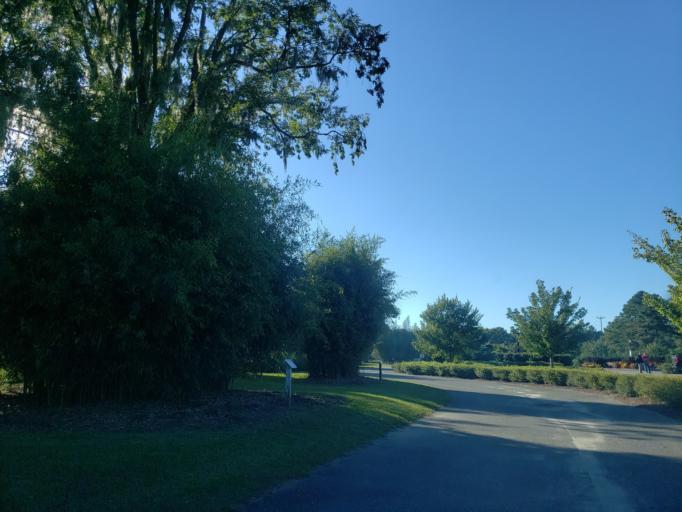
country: US
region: Georgia
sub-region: Chatham County
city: Georgetown
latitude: 31.9978
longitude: -81.2700
